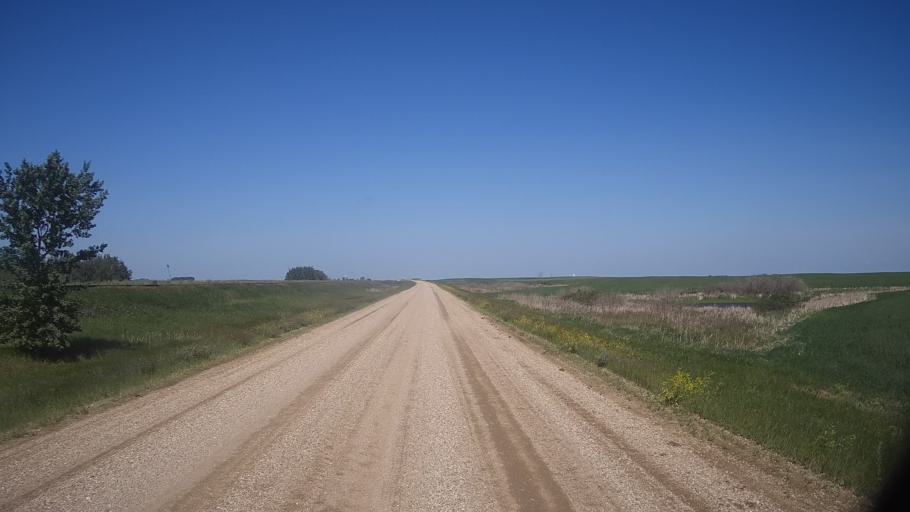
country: CA
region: Saskatchewan
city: Watrous
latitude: 51.8438
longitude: -105.9157
